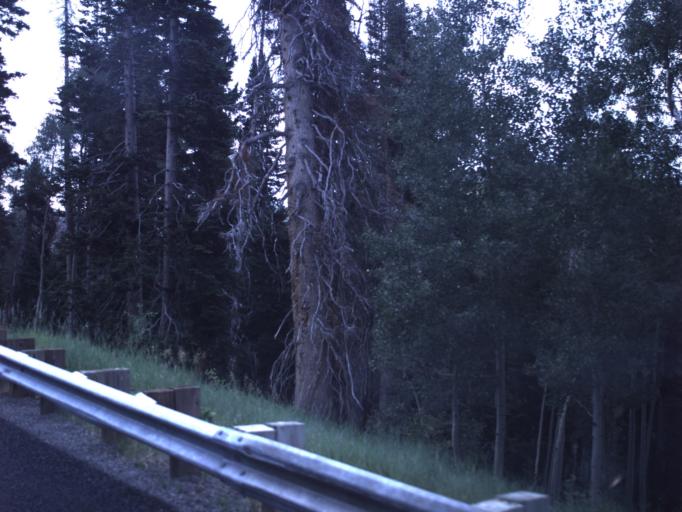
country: US
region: Utah
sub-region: Summit County
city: Francis
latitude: 40.4935
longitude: -111.0349
